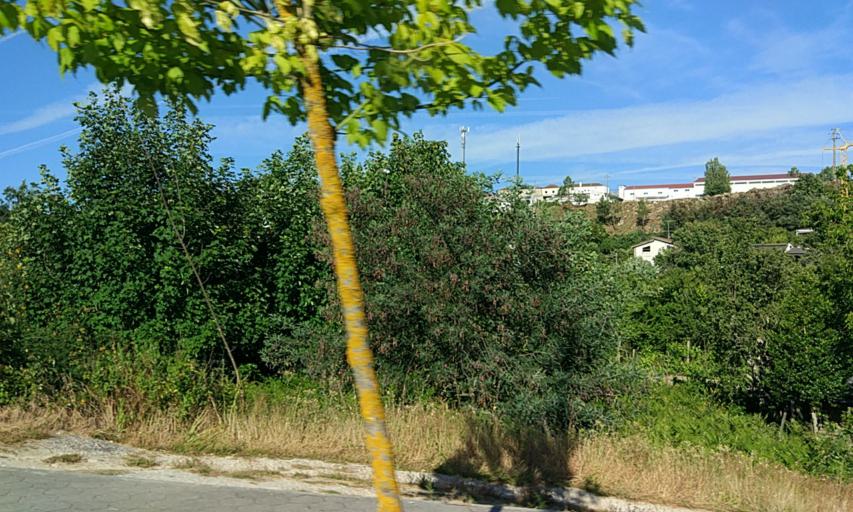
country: PT
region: Viseu
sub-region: Viseu
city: Abraveses
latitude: 40.6828
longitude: -7.9264
